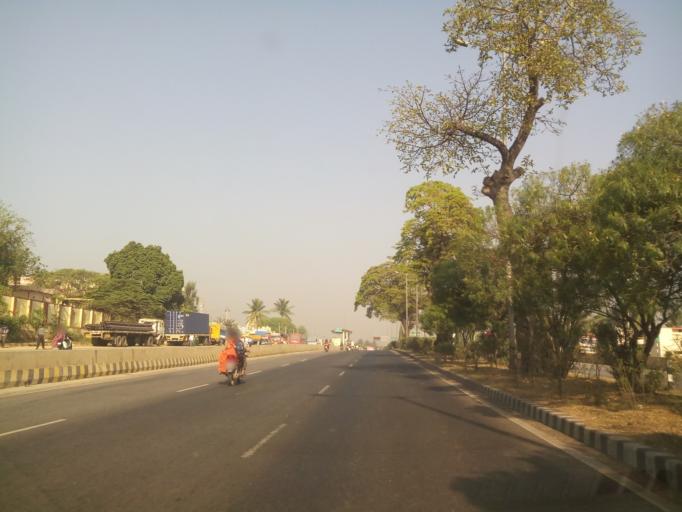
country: IN
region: Karnataka
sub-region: Bangalore Rural
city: Nelamangala
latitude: 13.0791
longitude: 77.4266
